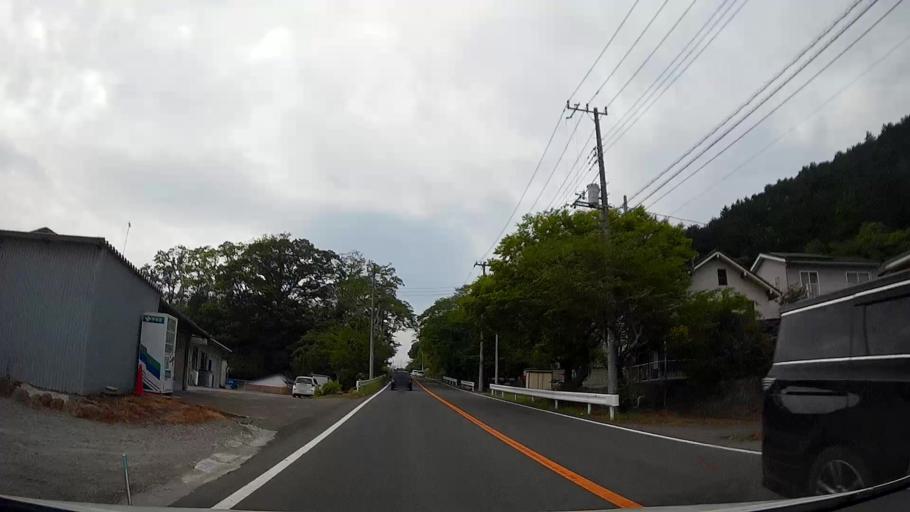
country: JP
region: Shizuoka
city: Ito
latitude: 34.9732
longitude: 138.9607
